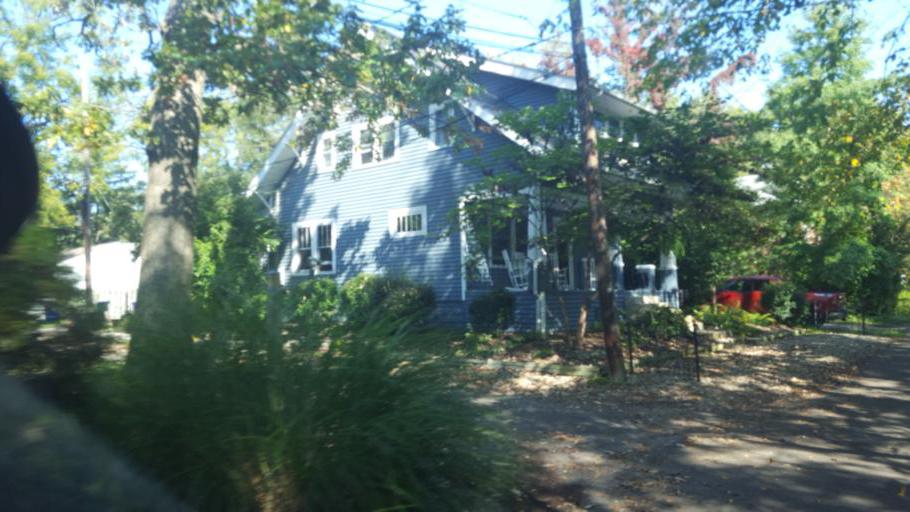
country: US
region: Ohio
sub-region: Franklin County
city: Grandview Heights
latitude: 40.0275
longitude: -83.0068
